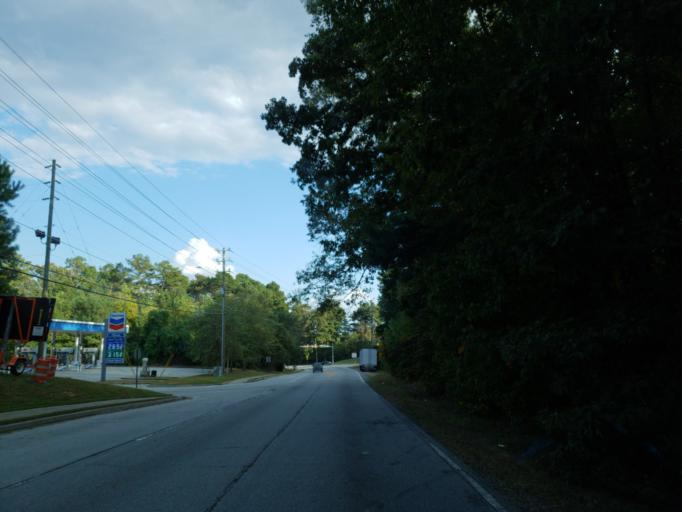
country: US
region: Georgia
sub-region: Cobb County
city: Mableton
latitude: 33.7526
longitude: -84.5820
